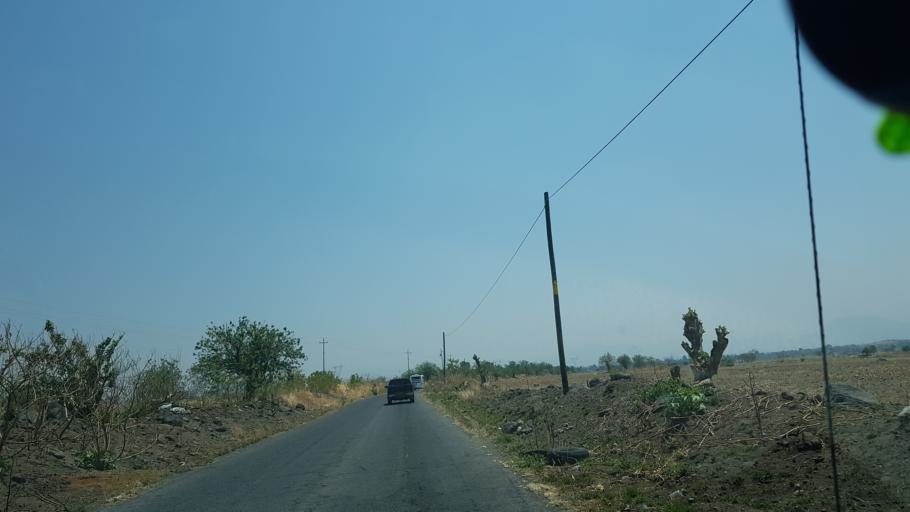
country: MX
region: Puebla
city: Tochimilco
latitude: 18.8874
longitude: -98.5391
